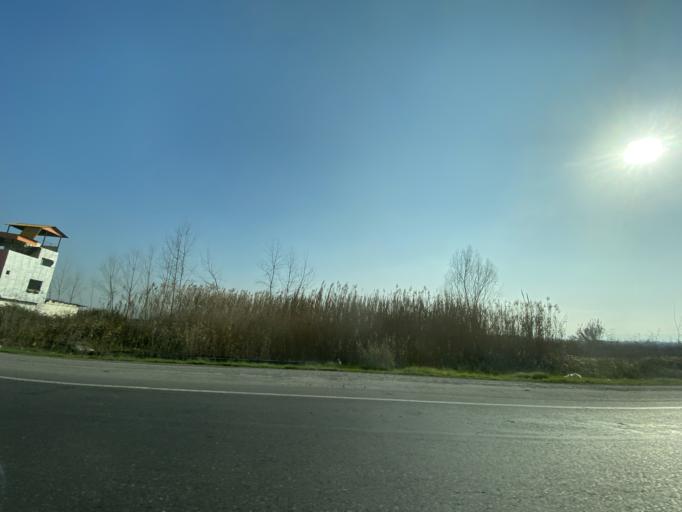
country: IR
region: Mazandaran
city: Amol
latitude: 36.4960
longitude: 52.5117
